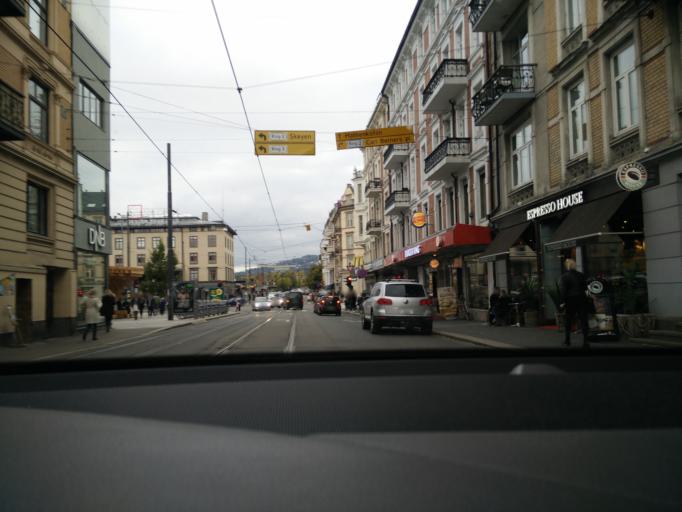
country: NO
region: Oslo
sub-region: Oslo
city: Oslo
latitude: 59.9288
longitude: 10.7177
